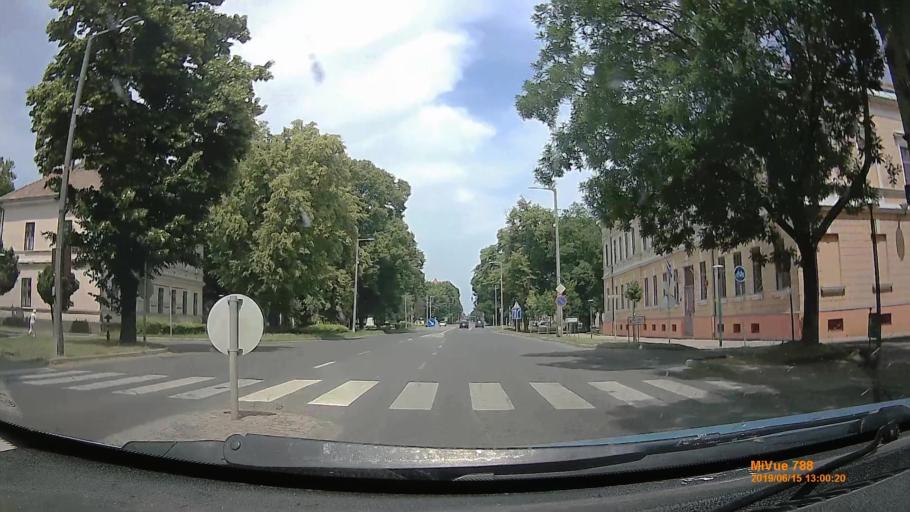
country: HU
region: Tolna
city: Dombovar
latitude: 46.3726
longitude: 18.1301
